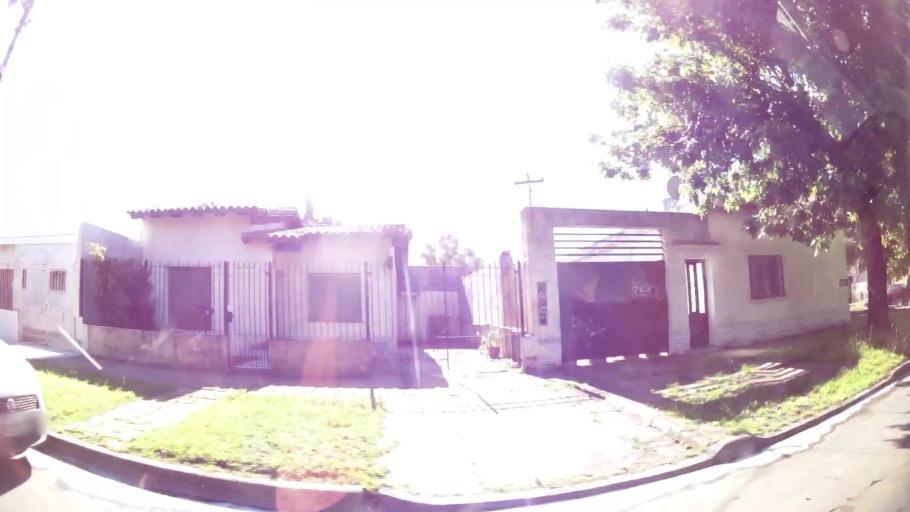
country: AR
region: Buenos Aires
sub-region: Partido de Lomas de Zamora
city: Lomas de Zamora
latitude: -34.7632
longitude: -58.4198
